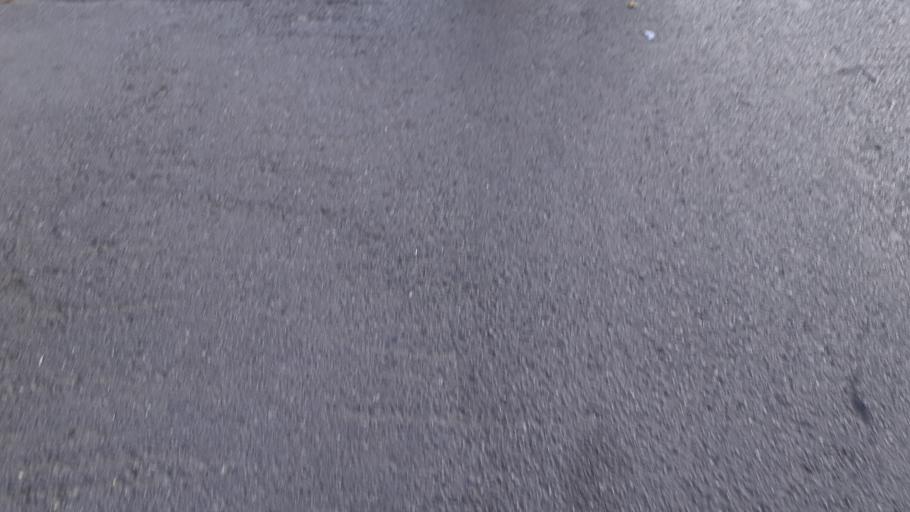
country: TR
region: Istanbul
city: Zeytinburnu
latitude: 41.0004
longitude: 28.9164
